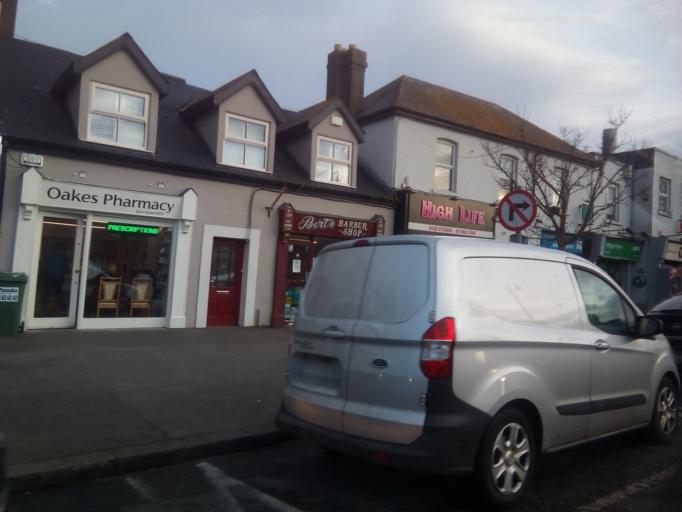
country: IE
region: Leinster
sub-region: Fingal County
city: Skerries
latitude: 53.5799
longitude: -6.1066
